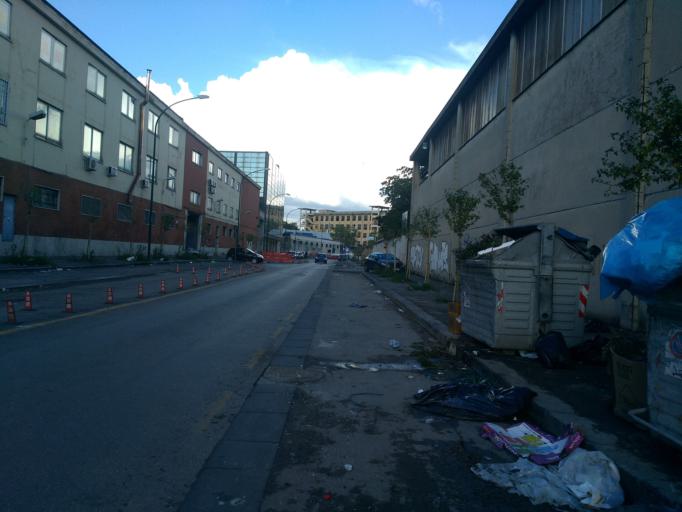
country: IT
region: Campania
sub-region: Provincia di Napoli
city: Napoli
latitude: 40.8475
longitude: 14.2906
